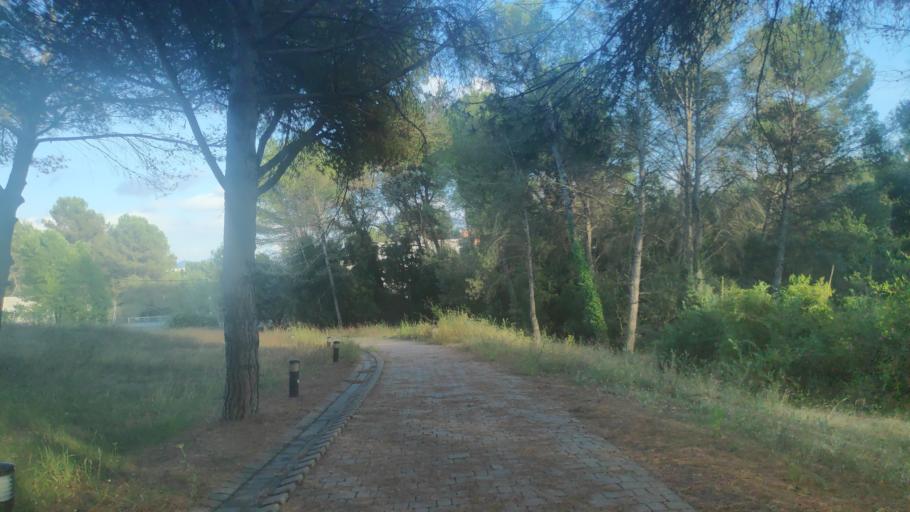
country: ES
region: Catalonia
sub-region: Provincia de Barcelona
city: Barbera del Valles
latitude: 41.5028
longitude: 2.1010
